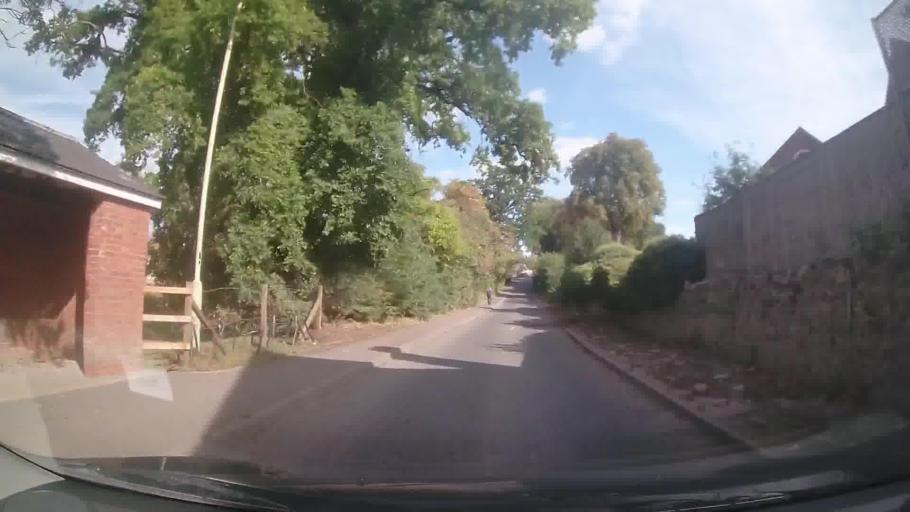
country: GB
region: England
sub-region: Shropshire
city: Pontesbury
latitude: 52.6504
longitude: -2.8900
